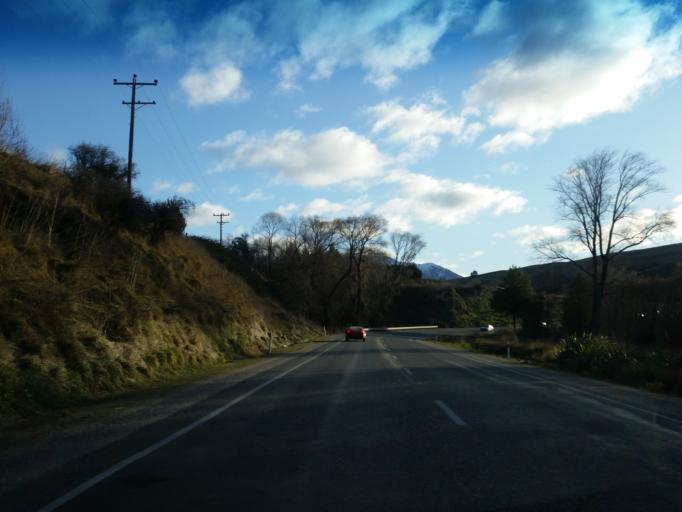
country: NZ
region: Otago
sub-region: Queenstown-Lakes District
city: Arrowtown
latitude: -44.9955
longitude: 168.8025
